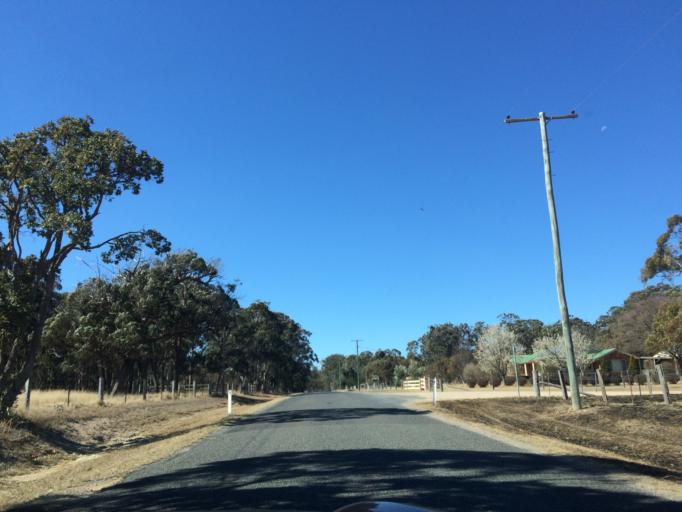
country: AU
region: Queensland
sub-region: Southern Downs
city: Stanthorpe
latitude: -28.6943
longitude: 152.0185
